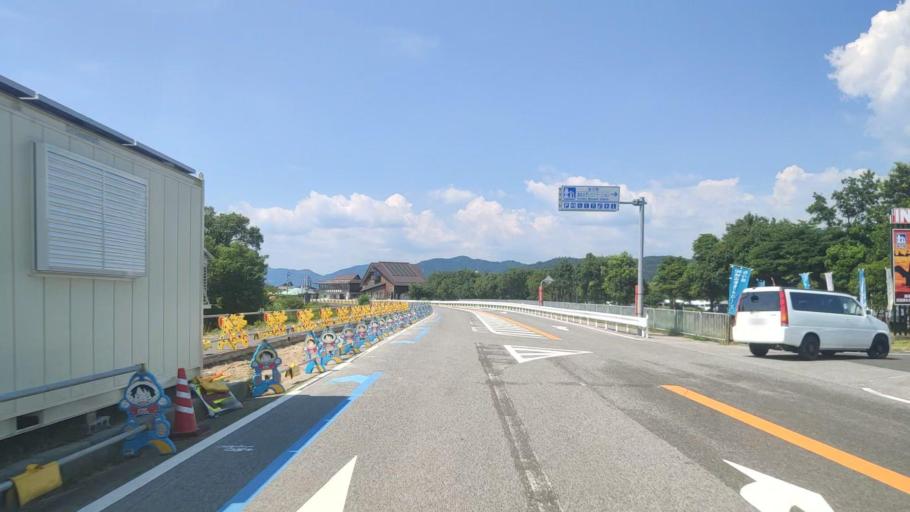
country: JP
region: Shiga Prefecture
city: Nagahama
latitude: 35.4444
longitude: 136.1898
